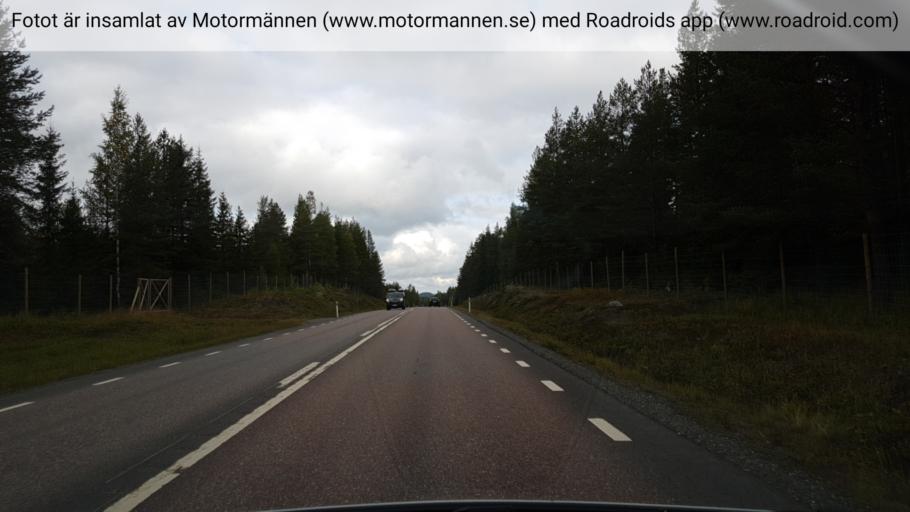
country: SE
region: Vaesterbotten
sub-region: Skelleftea Kommun
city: Viken
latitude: 64.8014
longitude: 20.7261
